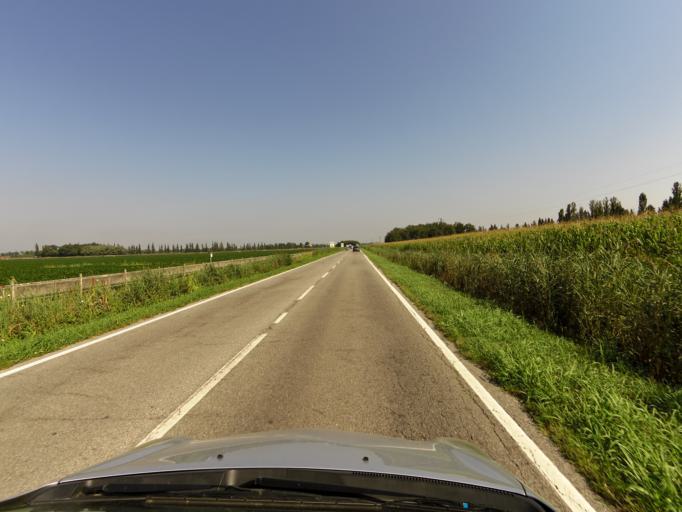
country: IT
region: Veneto
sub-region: Provincia di Venezia
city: La Salute di Livenza
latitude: 45.6110
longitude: 12.8029
